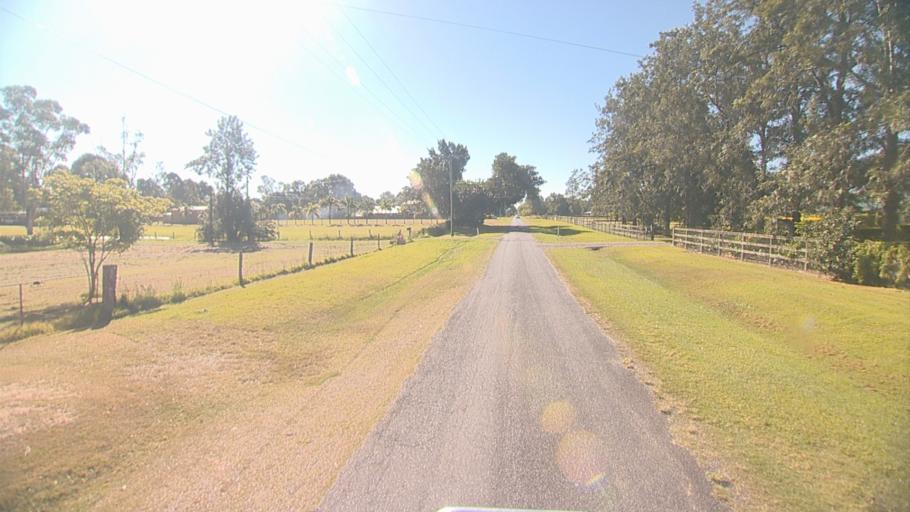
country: AU
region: Queensland
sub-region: Logan
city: Waterford West
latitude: -27.7192
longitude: 153.1260
